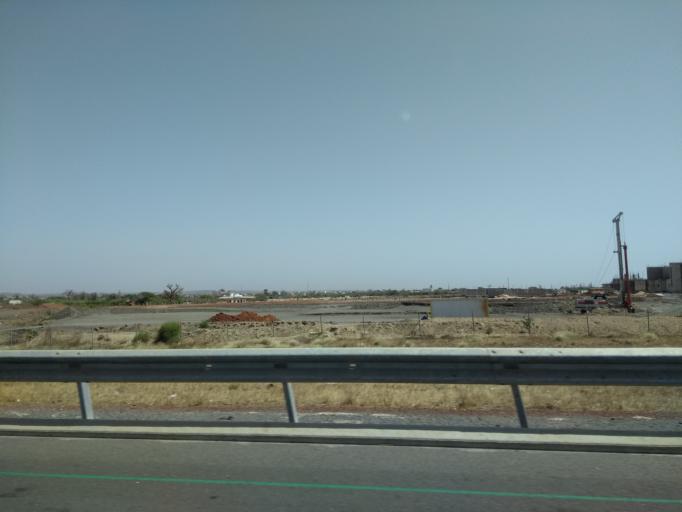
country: SN
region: Thies
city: Thies
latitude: 14.7372
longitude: -17.1953
